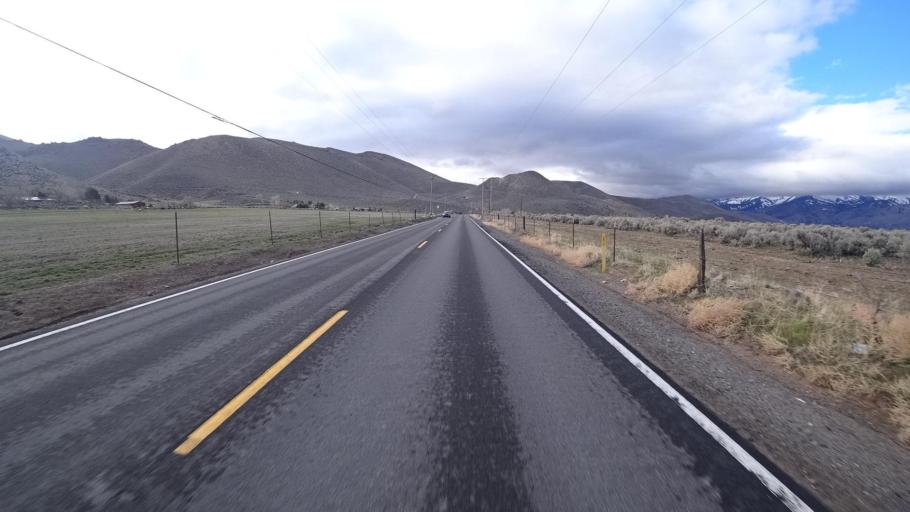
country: US
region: Nevada
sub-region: Carson City
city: Carson City
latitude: 39.2507
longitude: -119.7567
